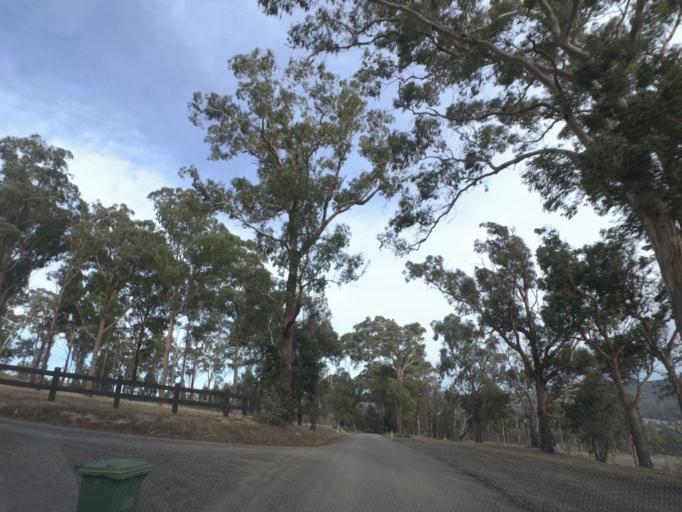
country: AU
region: Victoria
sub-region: Yarra Ranges
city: Yarra Glen
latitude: -37.5959
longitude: 145.3879
